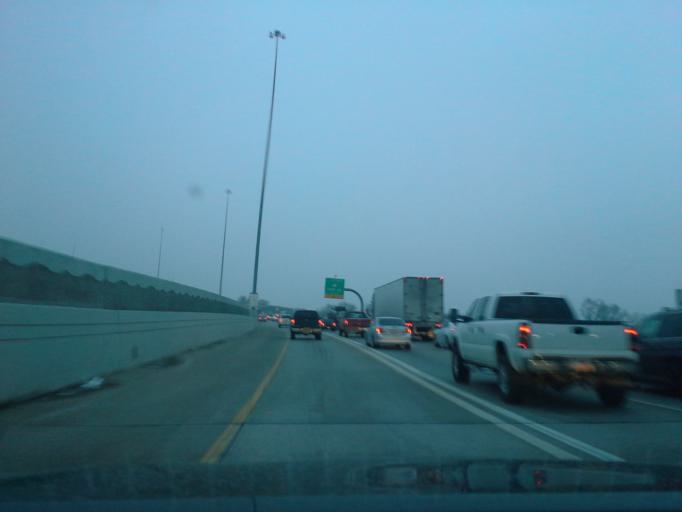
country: US
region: Utah
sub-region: Salt Lake County
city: Midvale
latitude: 40.6367
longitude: -111.9047
